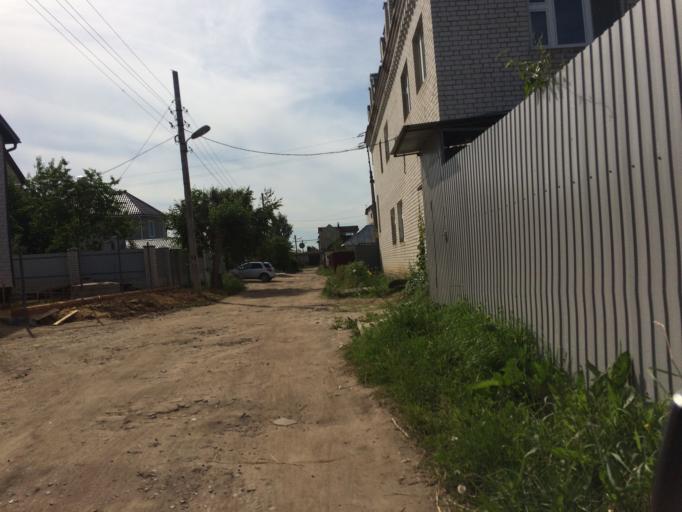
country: RU
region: Mariy-El
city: Yoshkar-Ola
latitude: 56.6519
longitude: 47.9167
